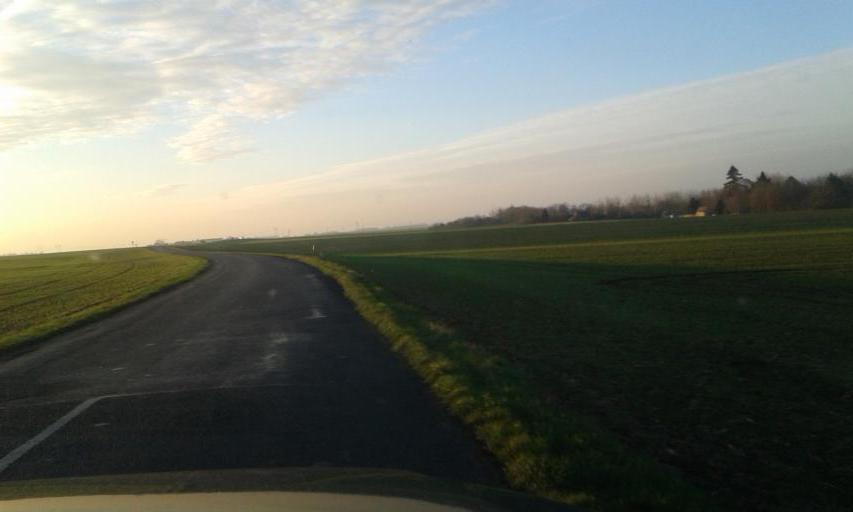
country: FR
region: Centre
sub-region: Departement du Loiret
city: Tavers
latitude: 47.7612
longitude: 1.5989
